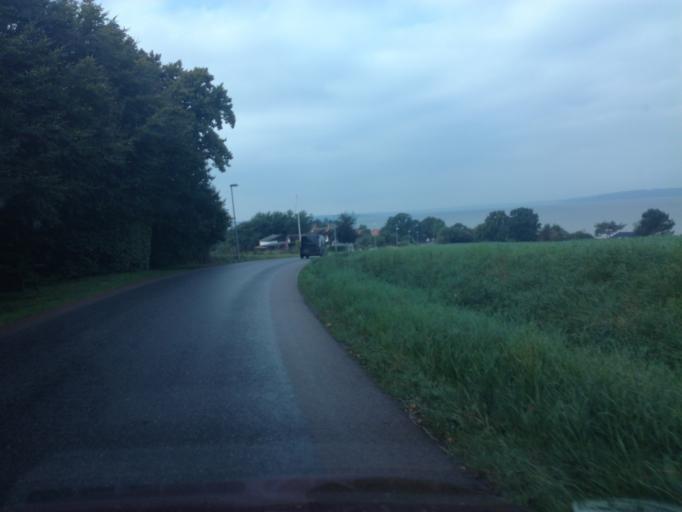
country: DK
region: South Denmark
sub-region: Fredericia Kommune
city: Fredericia
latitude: 55.6259
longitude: 9.8245
